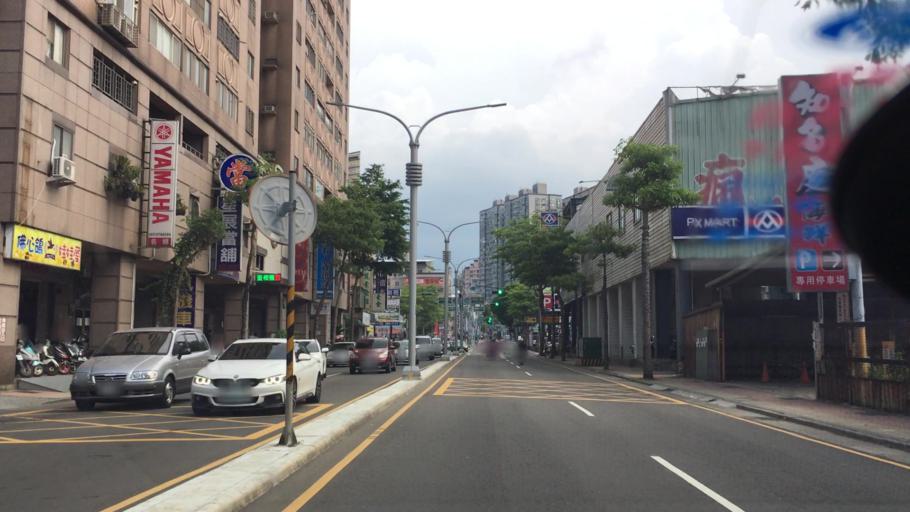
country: TW
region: Taiwan
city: Taoyuan City
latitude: 24.9939
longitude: 121.2881
